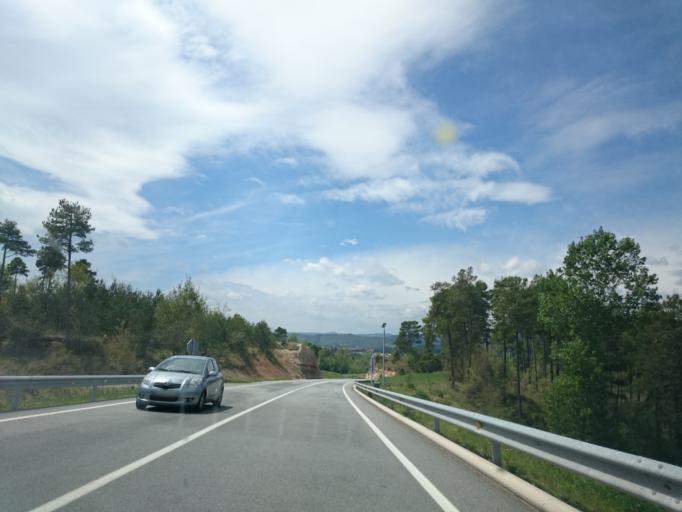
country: ES
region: Catalonia
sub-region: Provincia de Barcelona
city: Olvan
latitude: 42.0524
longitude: 1.9180
